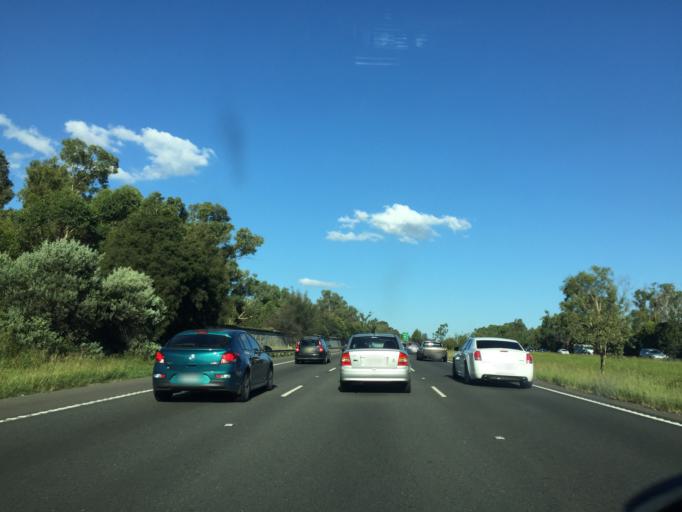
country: AU
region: New South Wales
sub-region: Blacktown
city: Mount Druitt
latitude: -33.7909
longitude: 150.8237
